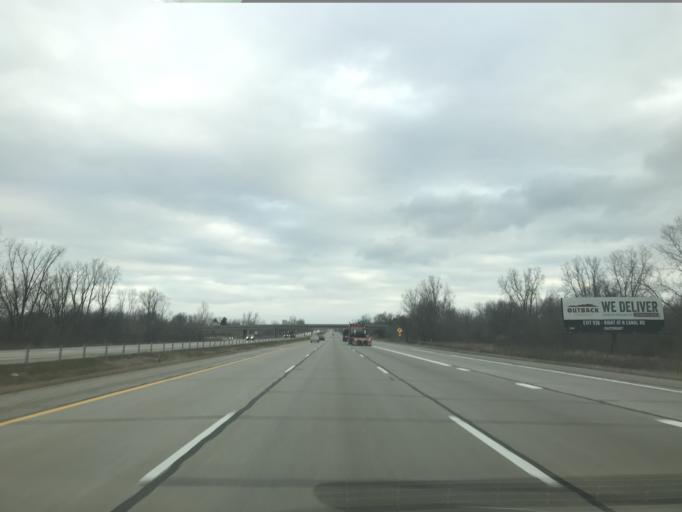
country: US
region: Michigan
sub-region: Eaton County
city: Waverly
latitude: 42.7089
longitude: -84.6693
